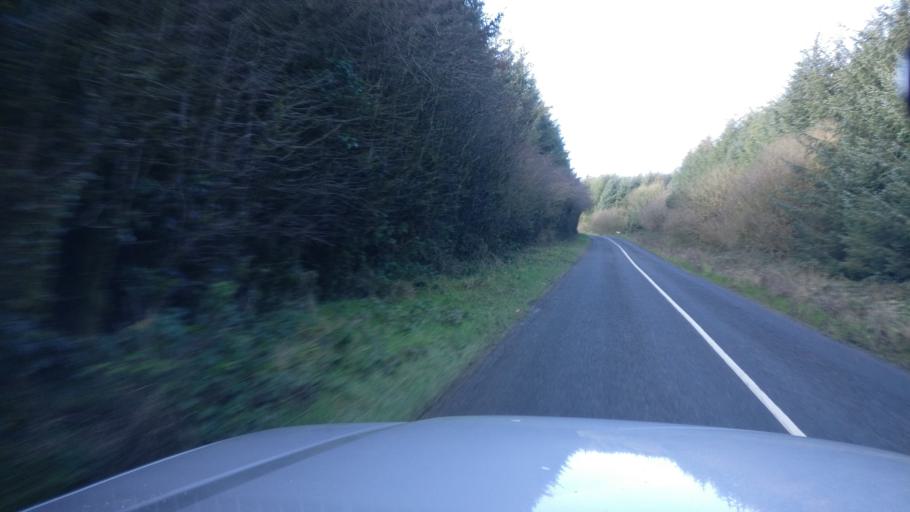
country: IE
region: Leinster
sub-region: Laois
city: Stradbally
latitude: 52.9136
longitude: -7.1836
